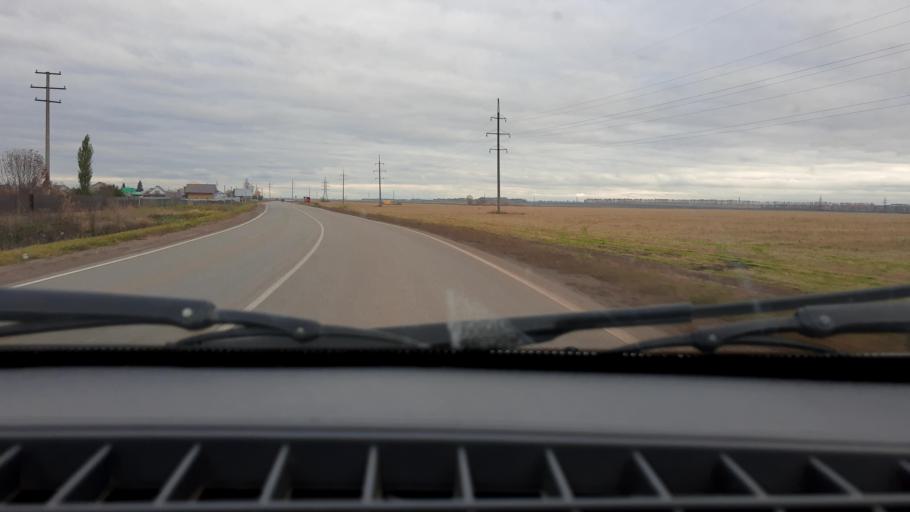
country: RU
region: Bashkortostan
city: Kabakovo
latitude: 54.5510
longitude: 56.0250
